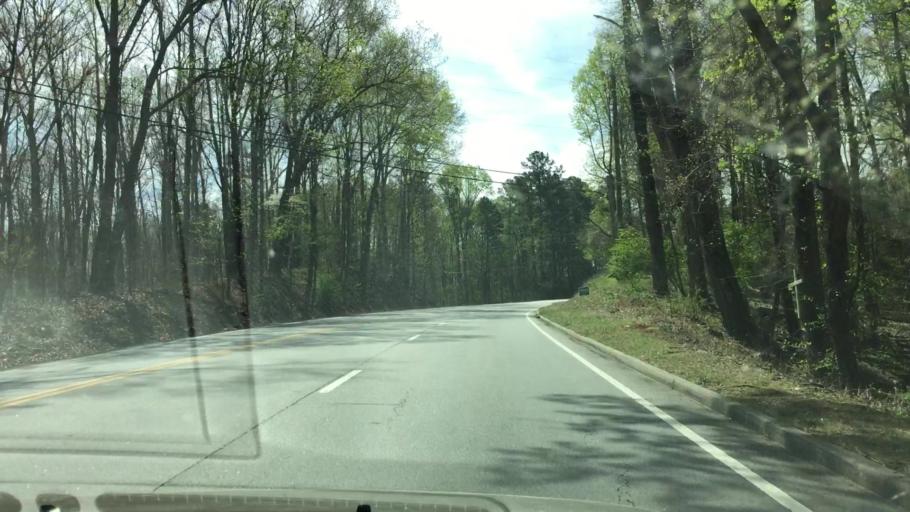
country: US
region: Georgia
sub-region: Barrow County
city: Winder
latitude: 34.0259
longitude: -83.7108
